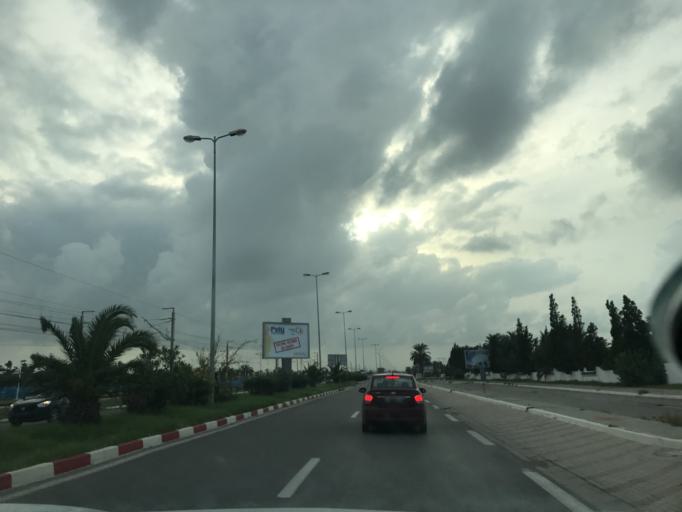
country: TN
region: Al Munastir
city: Sahline
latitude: 35.7626
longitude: 10.7538
